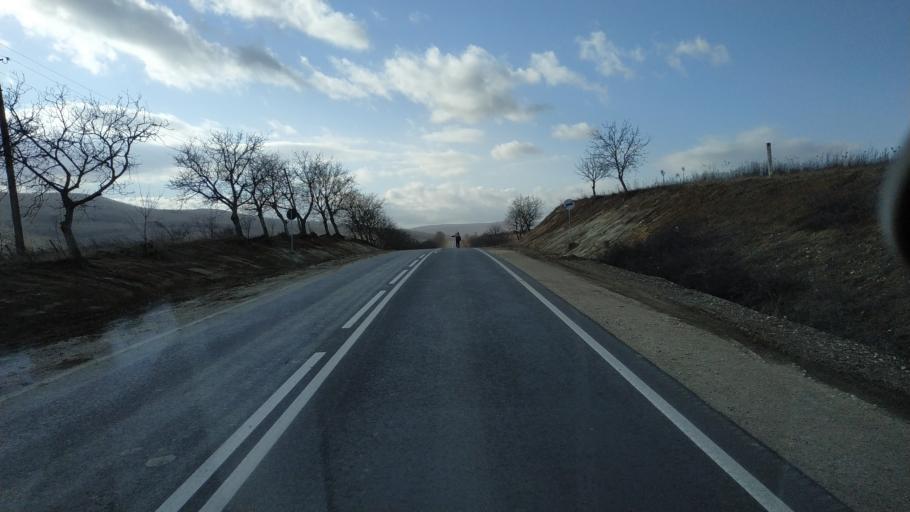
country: MD
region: Calarasi
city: Calarasi
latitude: 47.2956
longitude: 28.1619
